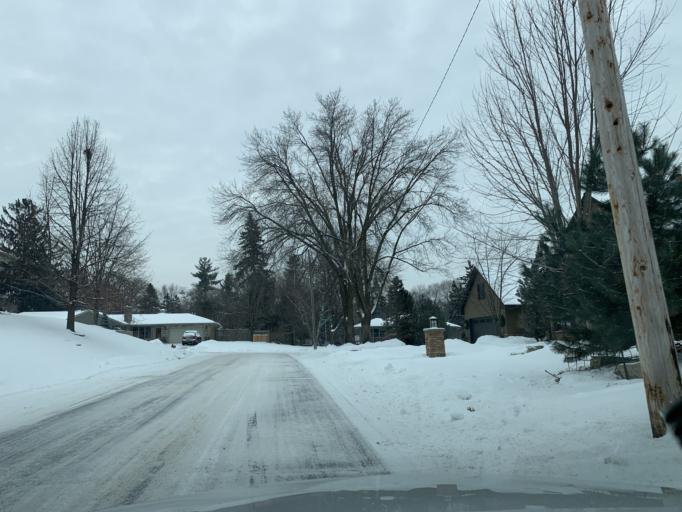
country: US
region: Minnesota
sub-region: Hennepin County
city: Edina
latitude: 44.9153
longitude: -93.3594
